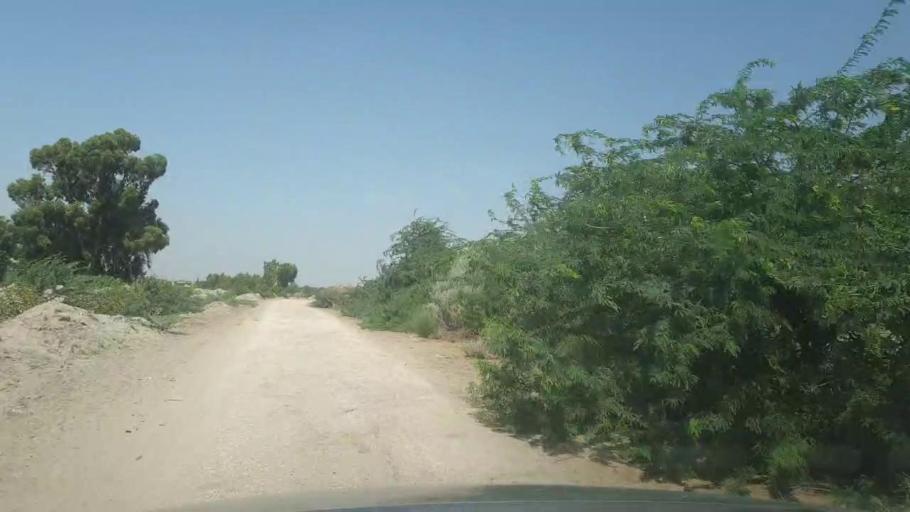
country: PK
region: Sindh
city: Khairpur
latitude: 27.4003
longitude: 69.0415
